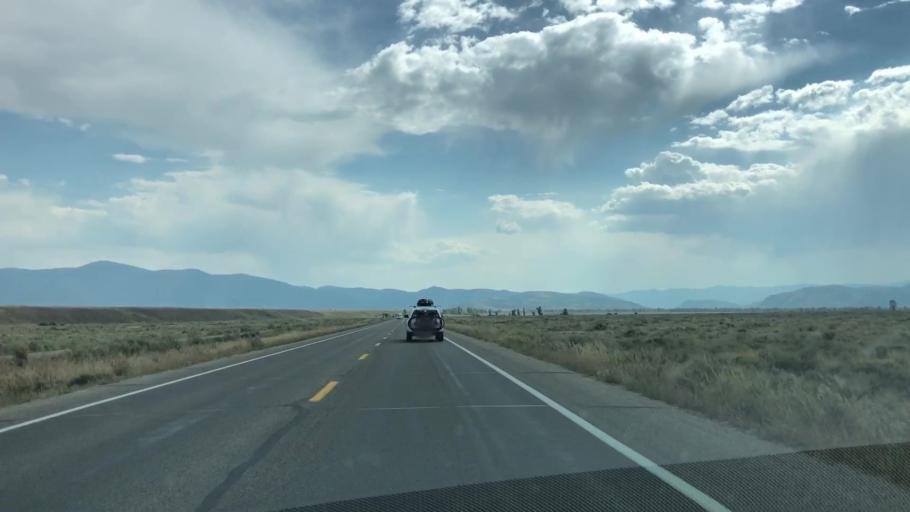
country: US
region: Wyoming
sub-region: Teton County
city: Jackson
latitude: 43.6059
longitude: -110.7234
